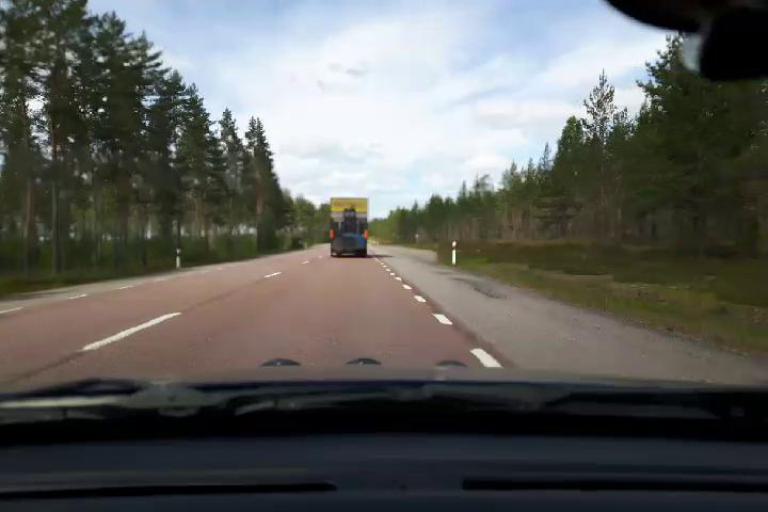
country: SE
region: Uppsala
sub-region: Osthammars Kommun
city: Bjorklinge
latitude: 60.1742
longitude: 17.4857
